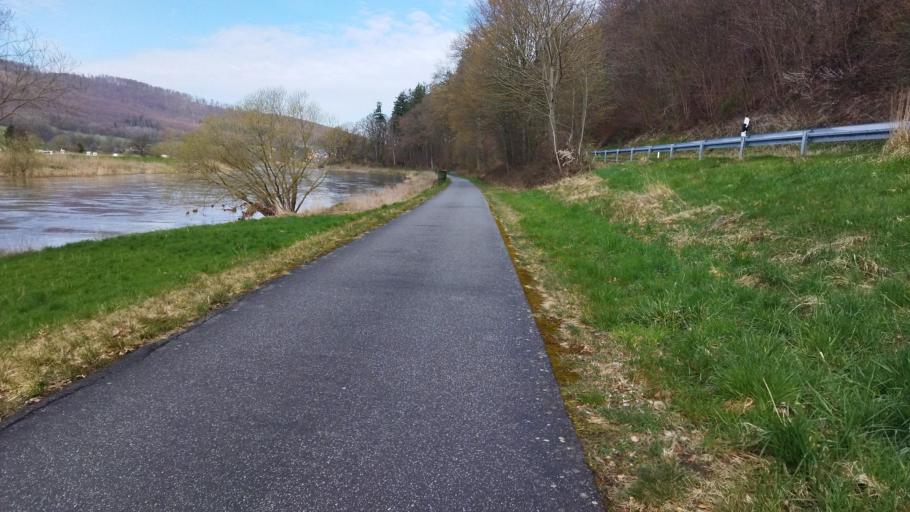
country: DE
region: Lower Saxony
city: Bodenfelde
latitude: 51.5645
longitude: 9.6039
